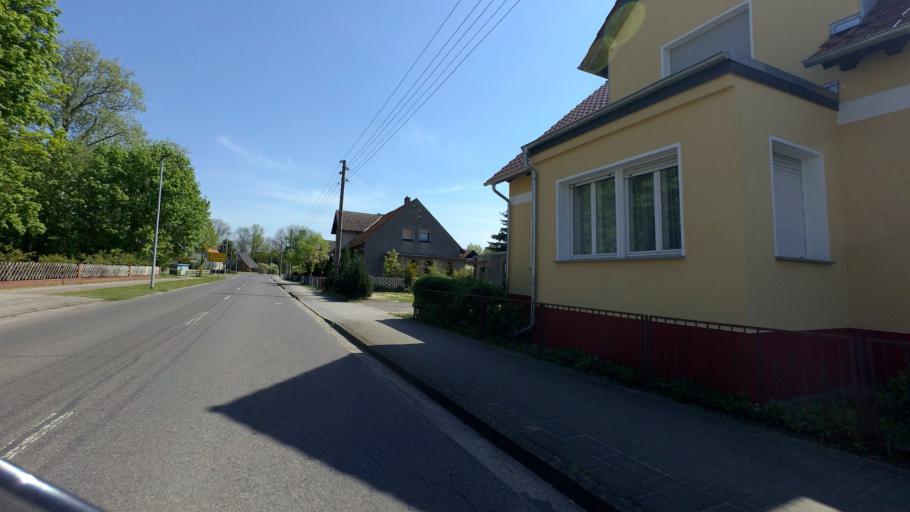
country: DE
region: Brandenburg
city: Schlepzig
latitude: 52.0533
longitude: 13.9902
